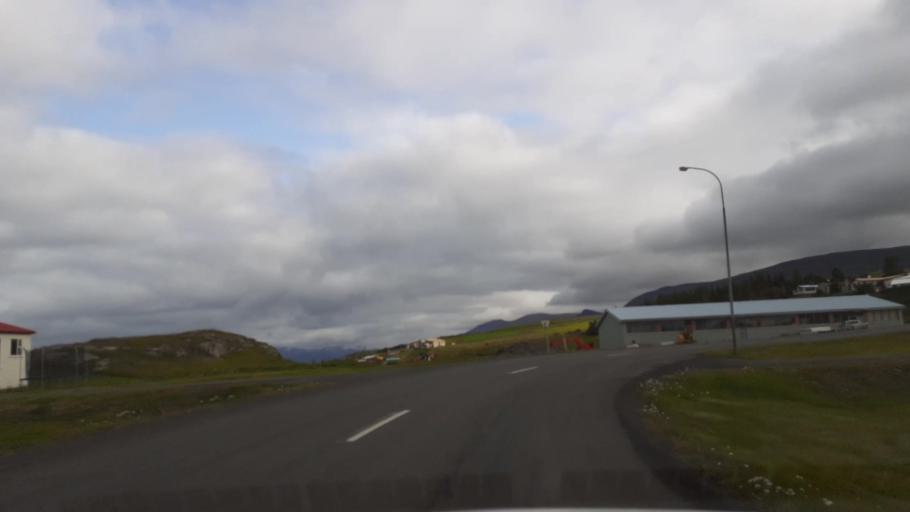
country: IS
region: Northeast
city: Akureyri
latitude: 65.7442
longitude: -18.0884
